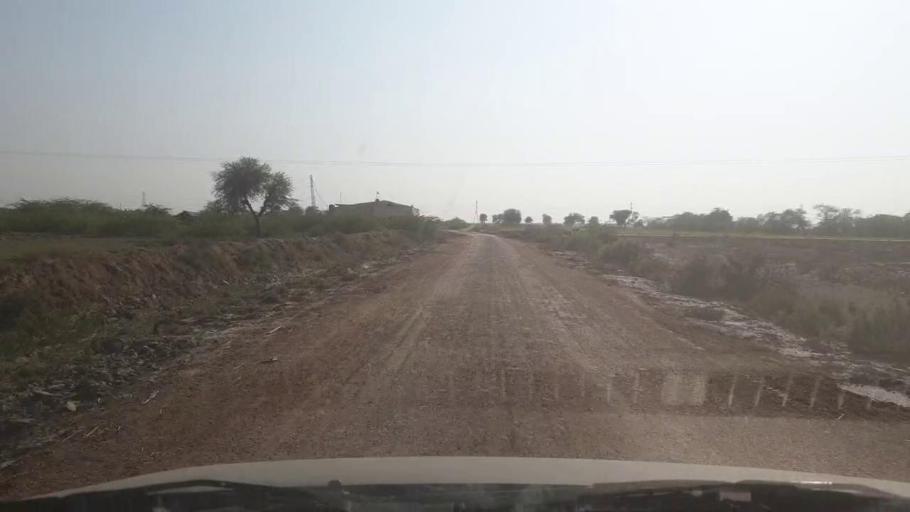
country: PK
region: Sindh
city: Samaro
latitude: 25.1406
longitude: 69.3768
